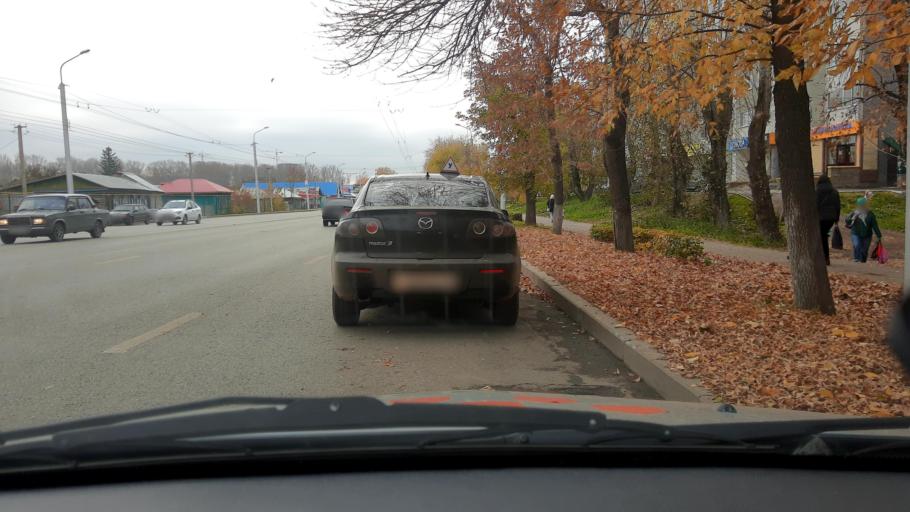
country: RU
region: Bashkortostan
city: Mikhaylovka
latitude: 54.7815
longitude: 55.8881
